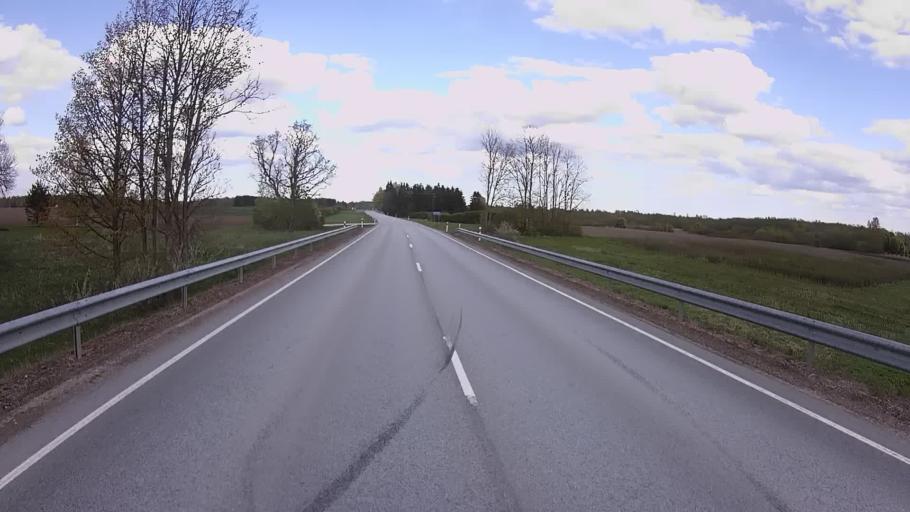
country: EE
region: Jogevamaa
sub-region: Jogeva linn
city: Jogeva
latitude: 58.8235
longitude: 26.6401
